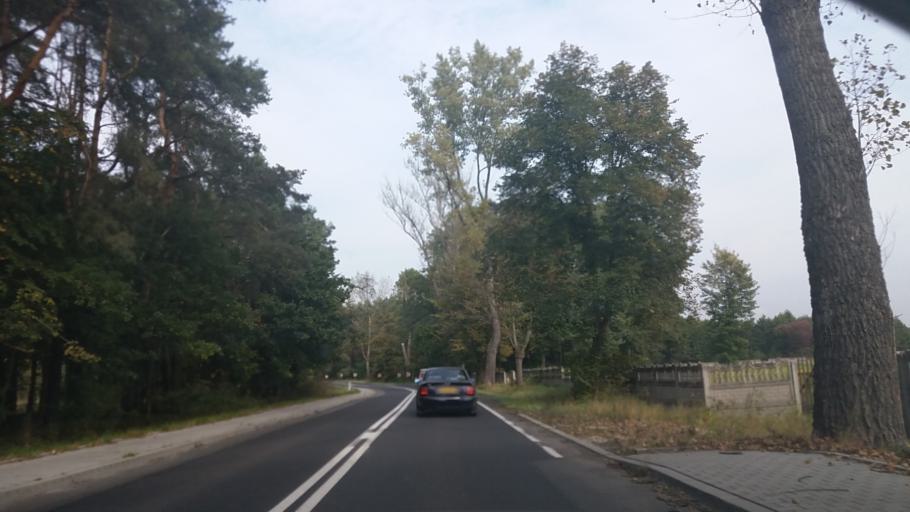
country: PL
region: Lesser Poland Voivodeship
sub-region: Powiat chrzanowski
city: Babice
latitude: 50.0575
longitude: 19.4535
